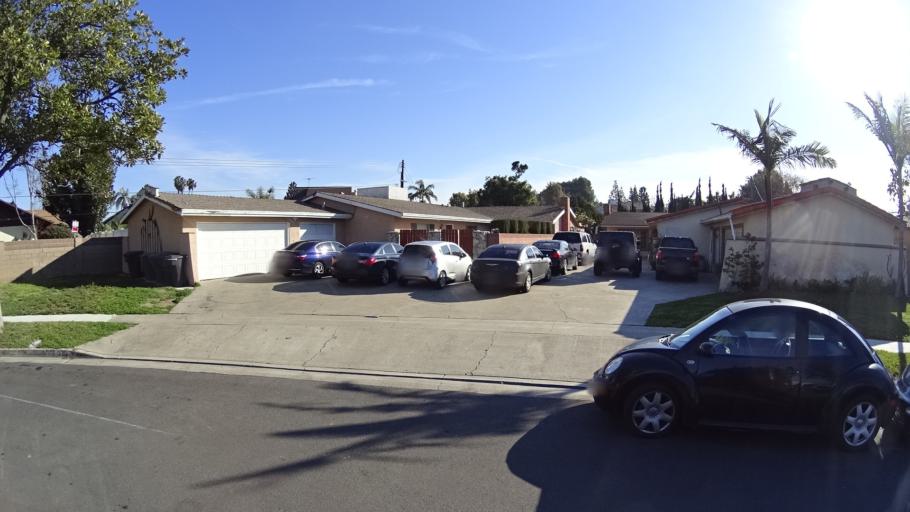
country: US
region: California
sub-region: Orange County
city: Anaheim
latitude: 33.8352
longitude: -117.9312
